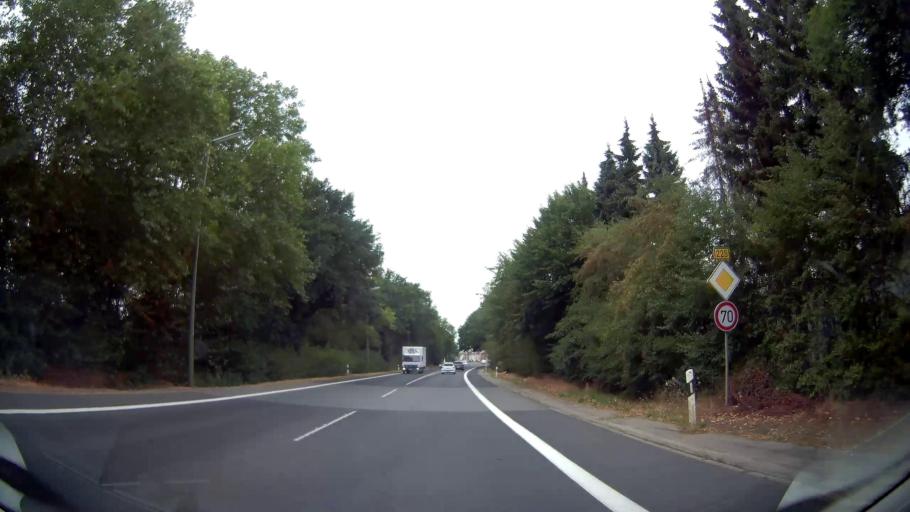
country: DE
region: North Rhine-Westphalia
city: Dorsten
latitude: 51.6564
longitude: 6.9884
